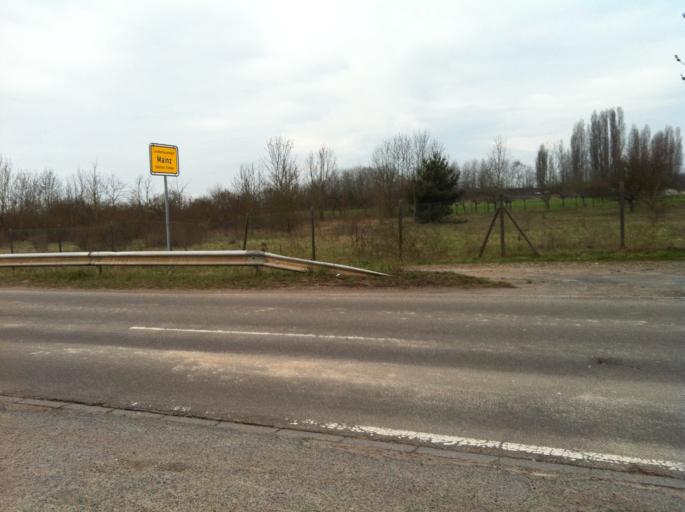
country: DE
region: Rheinland-Pfalz
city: Budenheim
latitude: 50.0013
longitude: 8.1731
